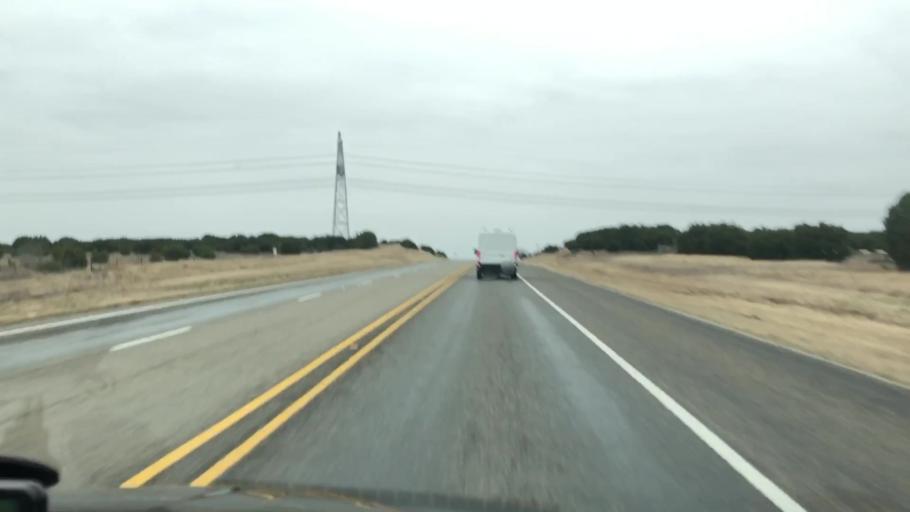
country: US
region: Texas
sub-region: Lampasas County
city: Lampasas
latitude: 31.1418
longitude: -98.1843
